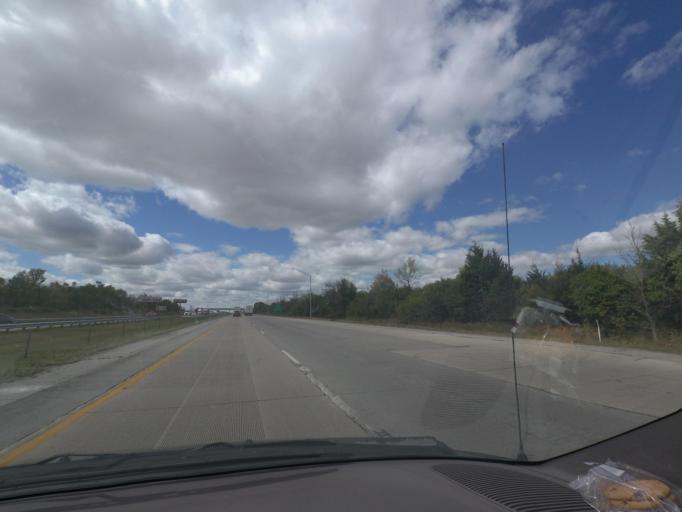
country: US
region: Indiana
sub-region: Wayne County
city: Richmond
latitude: 39.8668
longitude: -84.9347
